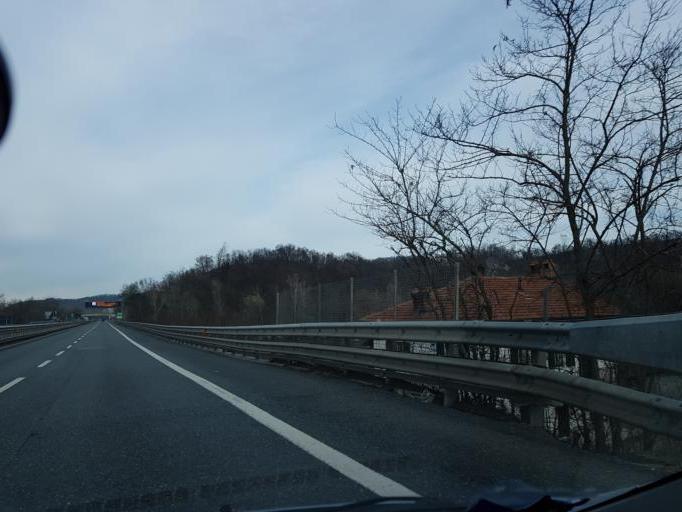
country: IT
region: Piedmont
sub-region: Provincia di Alessandria
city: Arquata Scrivia
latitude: 44.6912
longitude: 8.8998
